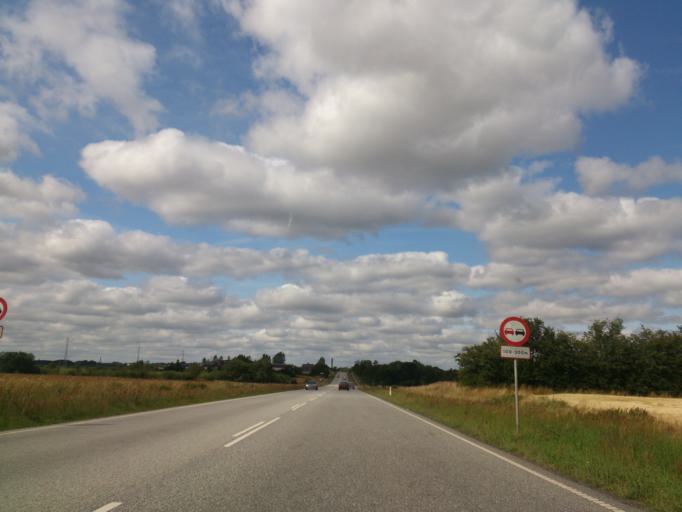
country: DK
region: South Denmark
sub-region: Aabenraa Kommune
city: Aabenraa
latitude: 54.9727
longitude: 9.4477
